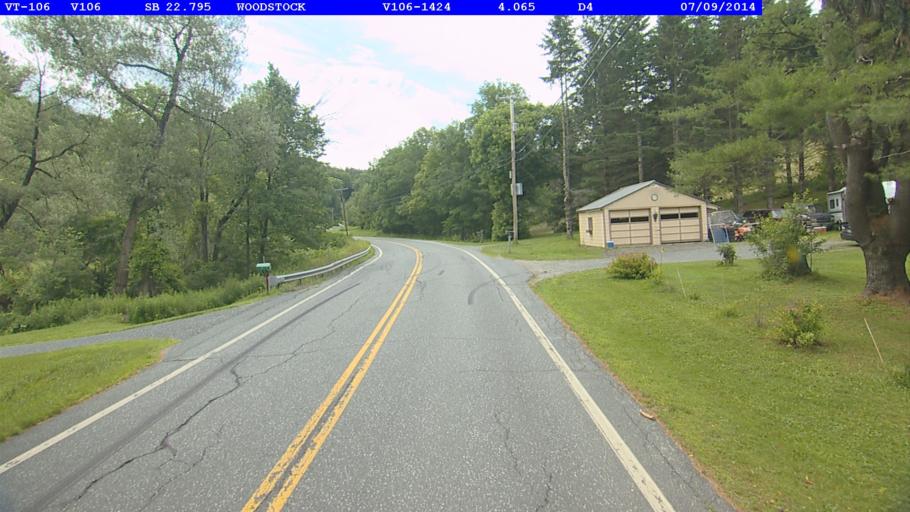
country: US
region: Vermont
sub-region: Windsor County
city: Woodstock
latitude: 43.5797
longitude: -72.5154
